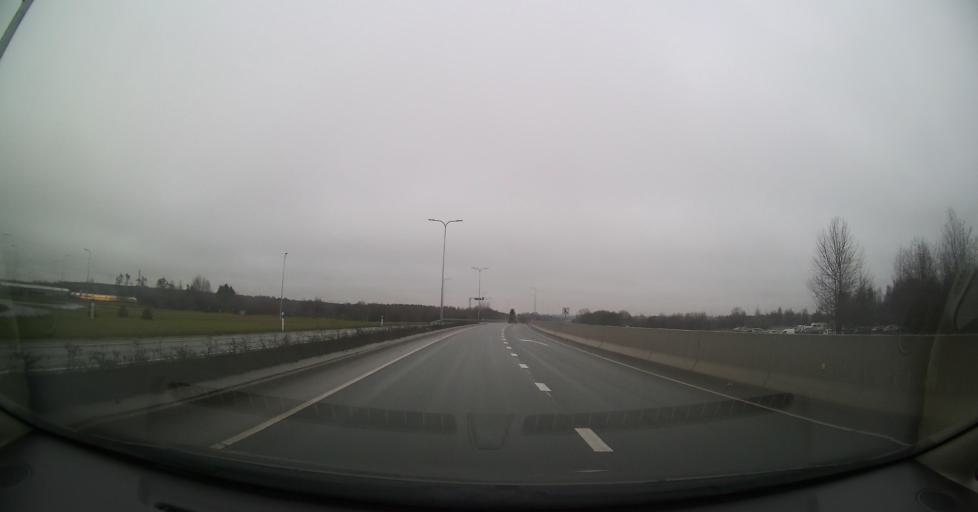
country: EE
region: Tartu
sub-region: Tartu linn
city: Tartu
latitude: 58.3736
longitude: 26.7800
